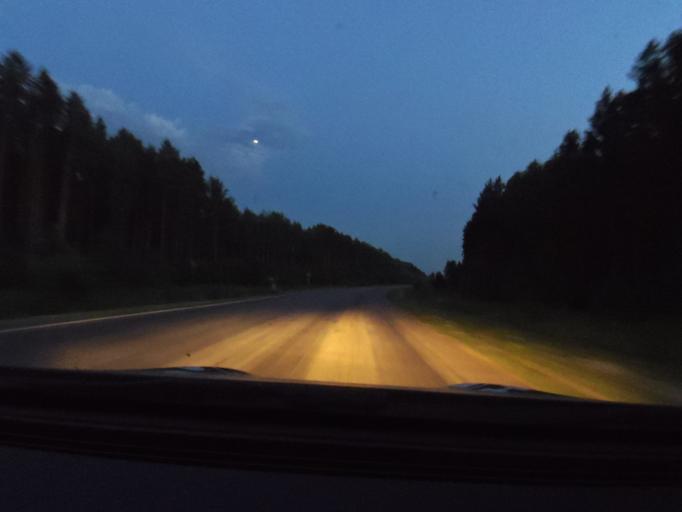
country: RU
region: Bashkortostan
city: Duvan
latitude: 55.9859
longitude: 58.2129
